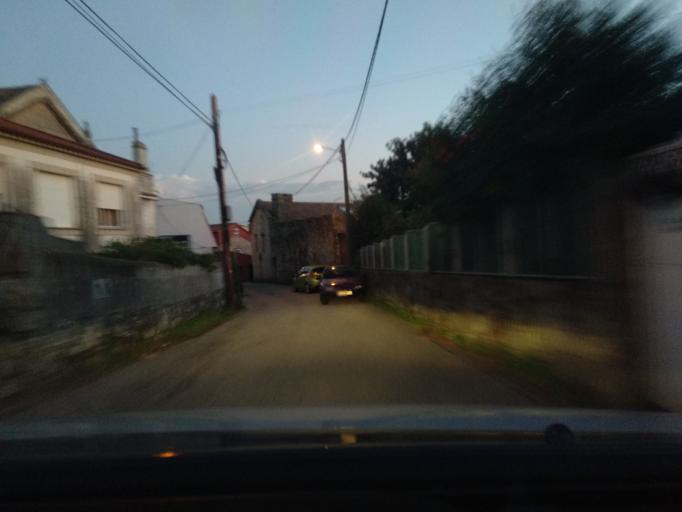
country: ES
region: Galicia
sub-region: Provincia de Pontevedra
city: Moana
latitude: 42.2823
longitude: -8.7468
